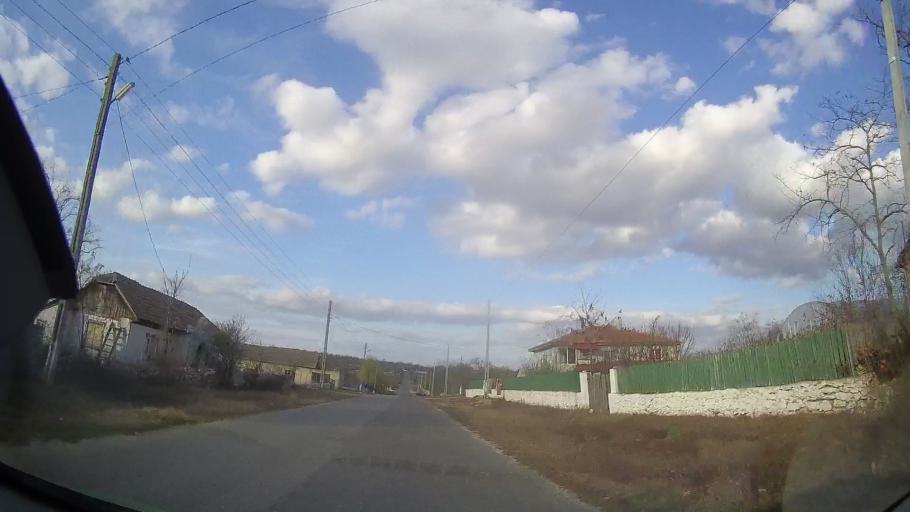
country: RO
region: Constanta
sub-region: Comuna Cerchezu
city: Cerchezu
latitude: 43.8547
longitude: 28.1012
